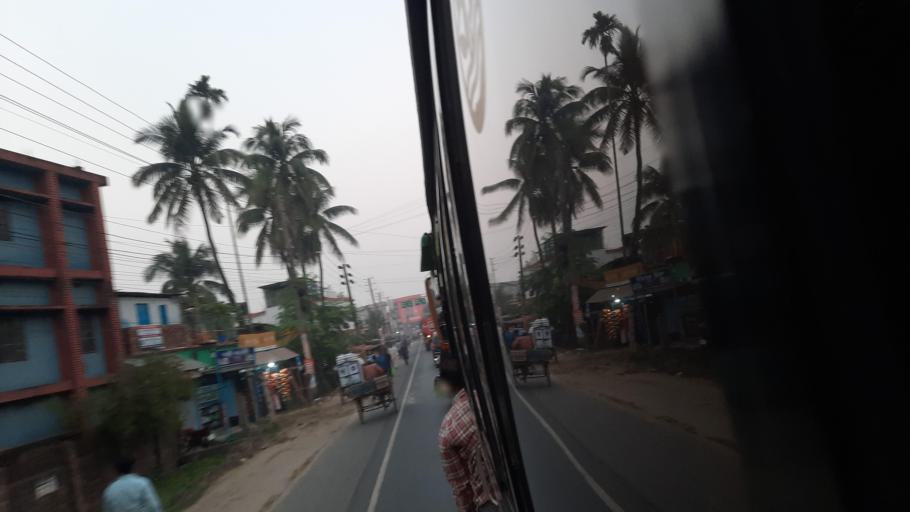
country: BD
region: Khulna
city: Jessore
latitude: 23.1789
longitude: 89.1914
